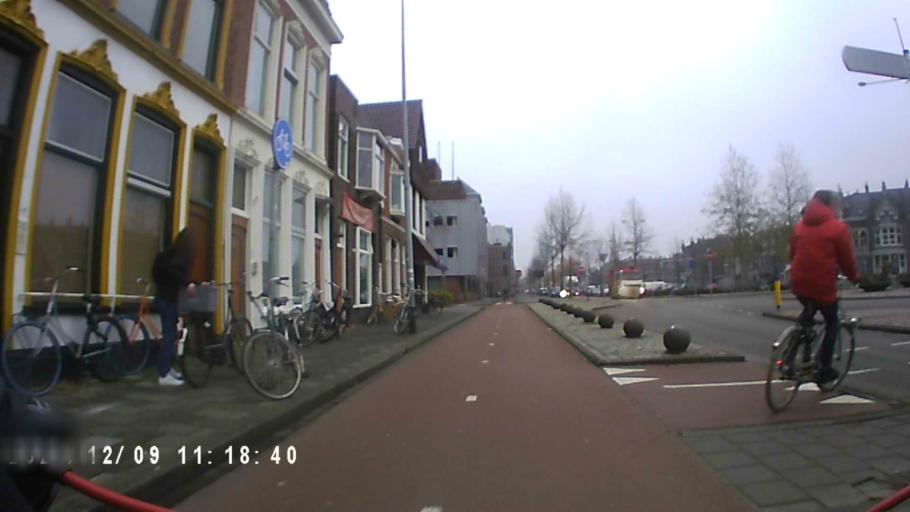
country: NL
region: Groningen
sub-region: Gemeente Groningen
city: Groningen
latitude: 53.2148
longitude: 6.5511
